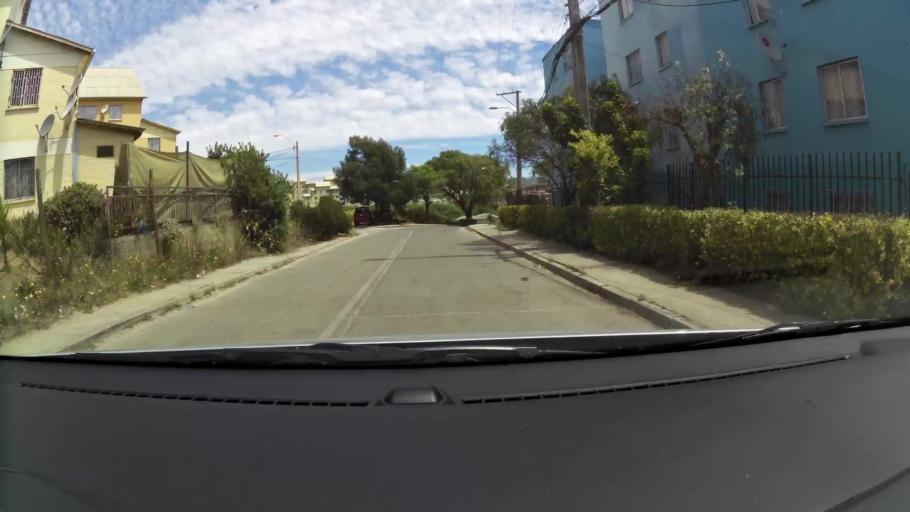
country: CL
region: Valparaiso
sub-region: Provincia de Valparaiso
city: Vina del Mar
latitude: -33.0591
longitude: -71.5592
